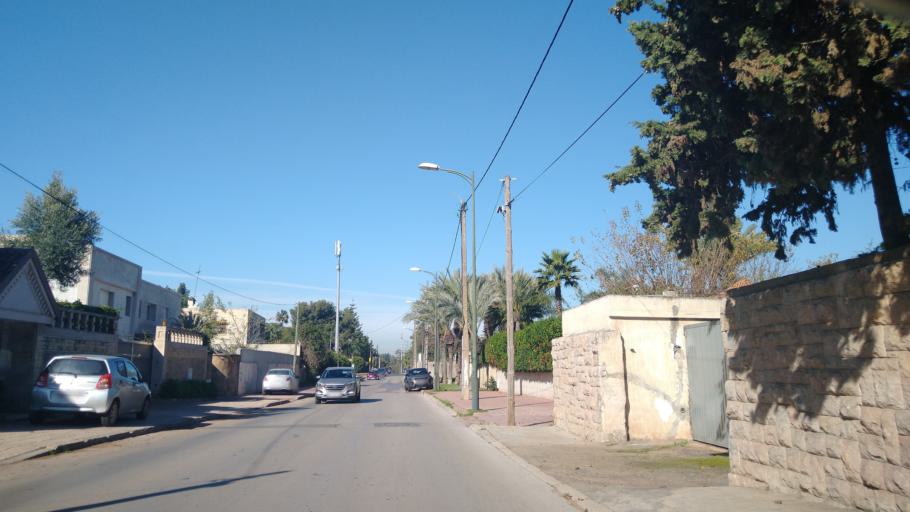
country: MA
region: Rabat-Sale-Zemmour-Zaer
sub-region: Rabat
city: Rabat
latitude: 33.9698
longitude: -6.8563
